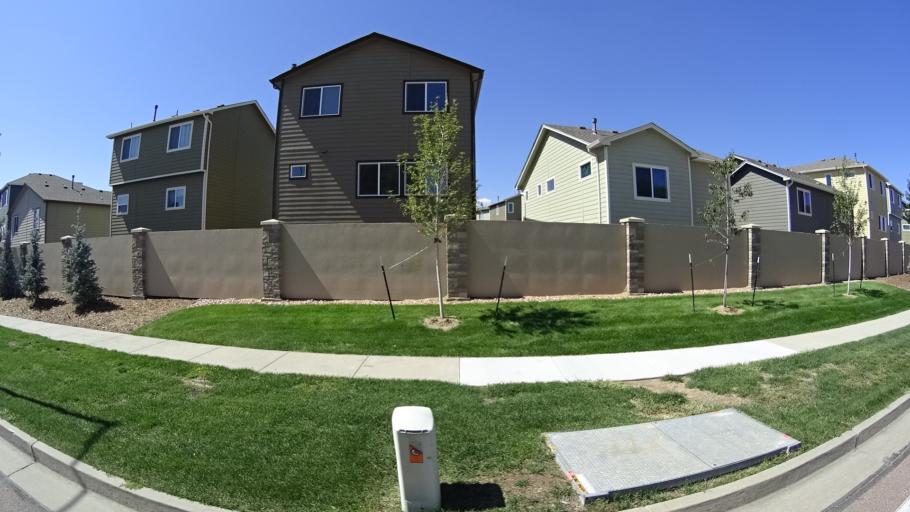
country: US
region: Colorado
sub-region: El Paso County
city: Cimarron Hills
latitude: 38.8446
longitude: -104.7228
